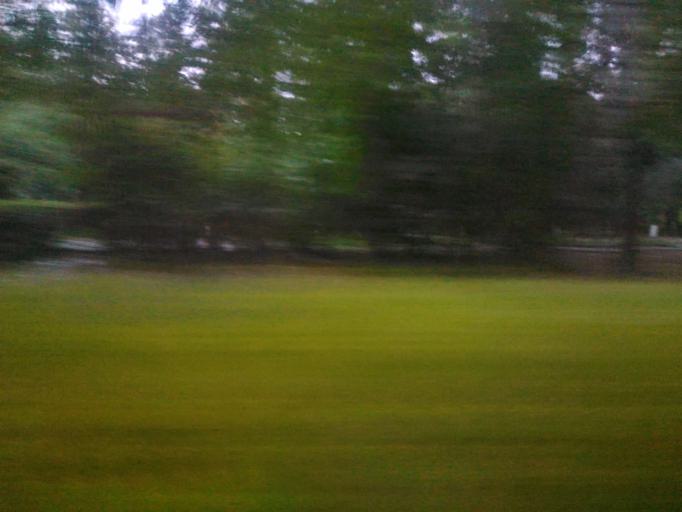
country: RU
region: Ulyanovsk
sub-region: Ulyanovskiy Rayon
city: Ulyanovsk
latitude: 54.3033
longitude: 48.3227
